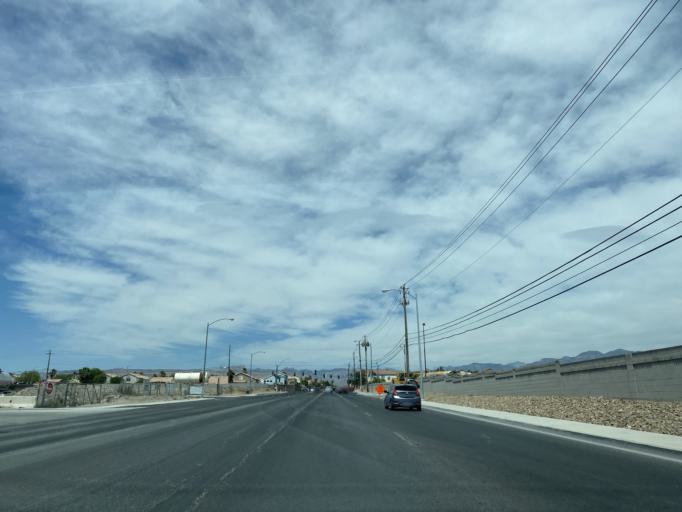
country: US
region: Nevada
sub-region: Clark County
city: Spring Valley
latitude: 36.1256
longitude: -115.2585
